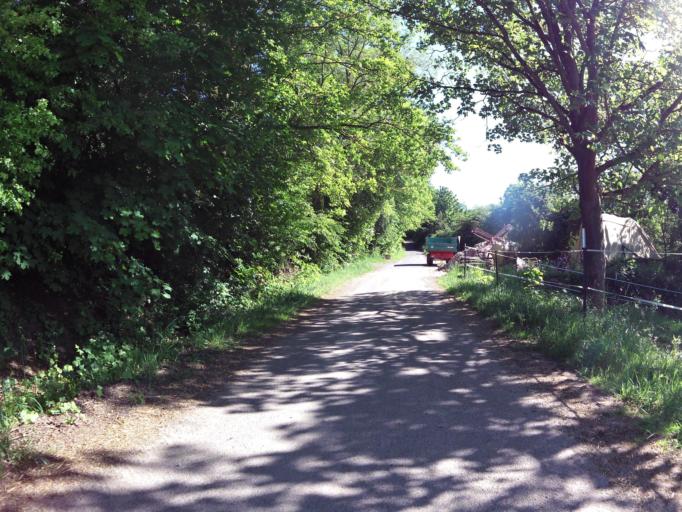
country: DE
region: Hesse
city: Philippsthal
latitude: 50.8325
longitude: 9.9941
